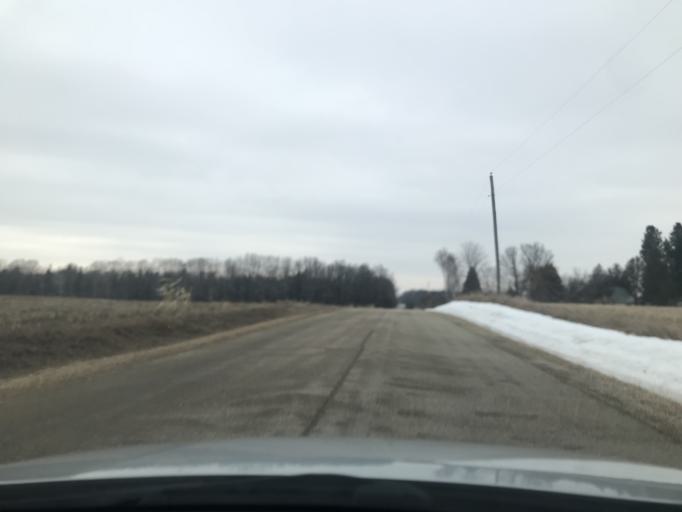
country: US
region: Wisconsin
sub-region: Marinette County
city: Peshtigo
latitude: 45.1220
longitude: -88.0082
